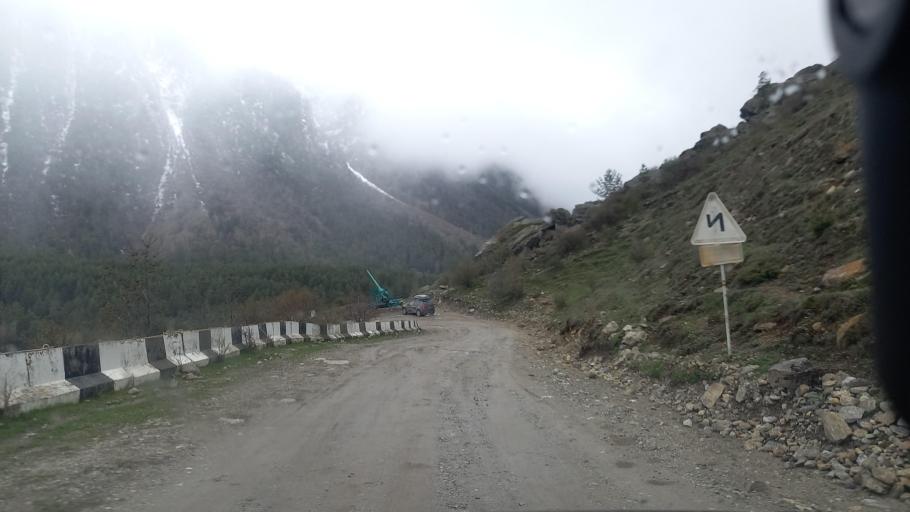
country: RU
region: Kabardino-Balkariya
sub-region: El'brusskiy Rayon
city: El'brus
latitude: 43.2269
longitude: 42.6633
